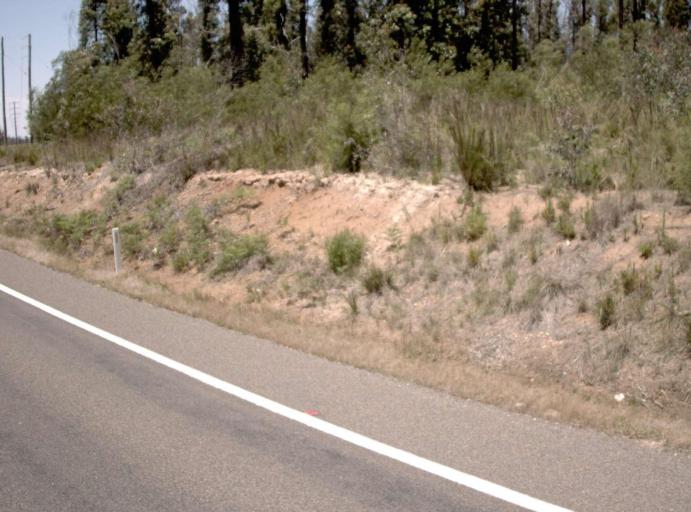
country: AU
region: Victoria
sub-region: East Gippsland
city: Lakes Entrance
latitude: -37.7486
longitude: 148.2248
